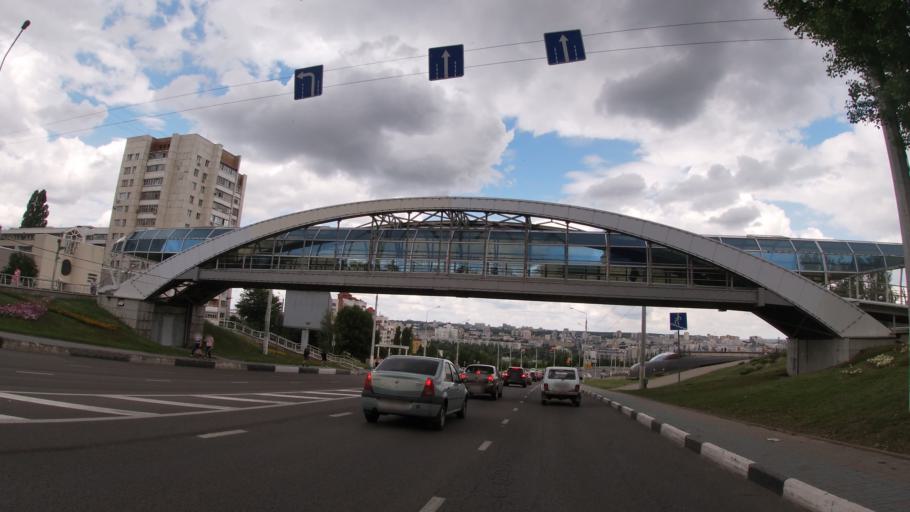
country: RU
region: Belgorod
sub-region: Belgorodskiy Rayon
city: Belgorod
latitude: 50.5799
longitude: 36.5831
